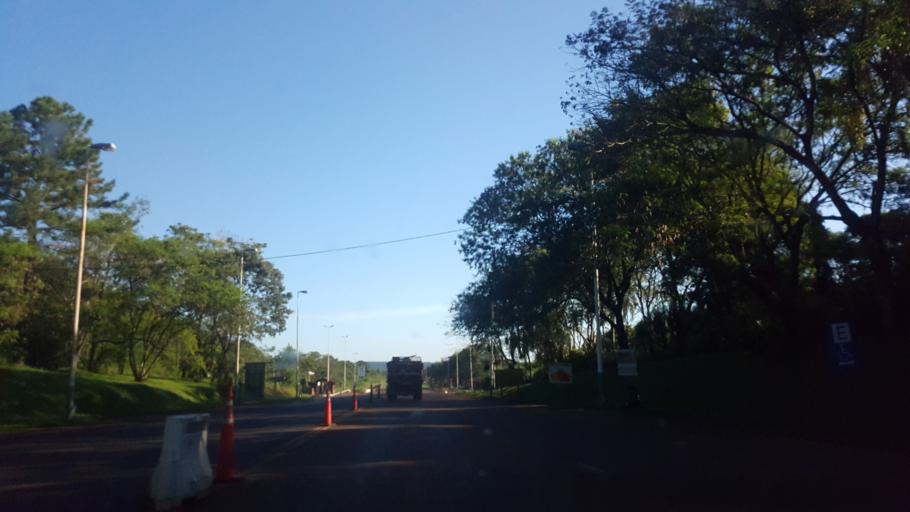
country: AR
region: Misiones
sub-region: Departamento de Eldorado
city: Eldorado
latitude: -26.3363
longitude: -54.6176
